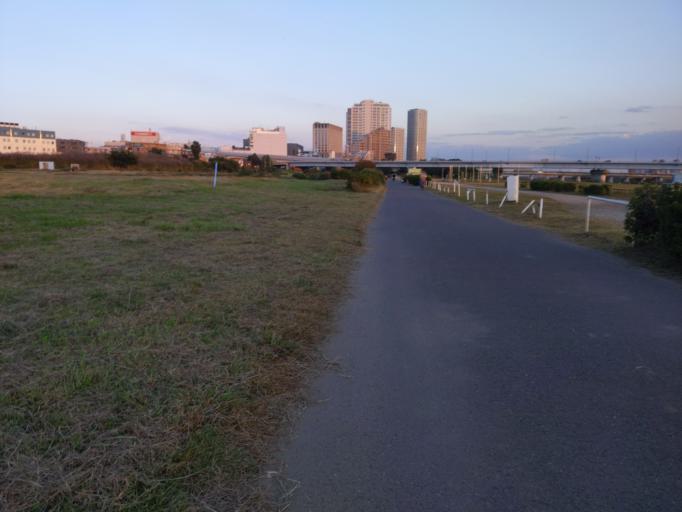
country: JP
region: Tokyo
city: Chofugaoka
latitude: 35.6144
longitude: 139.6185
